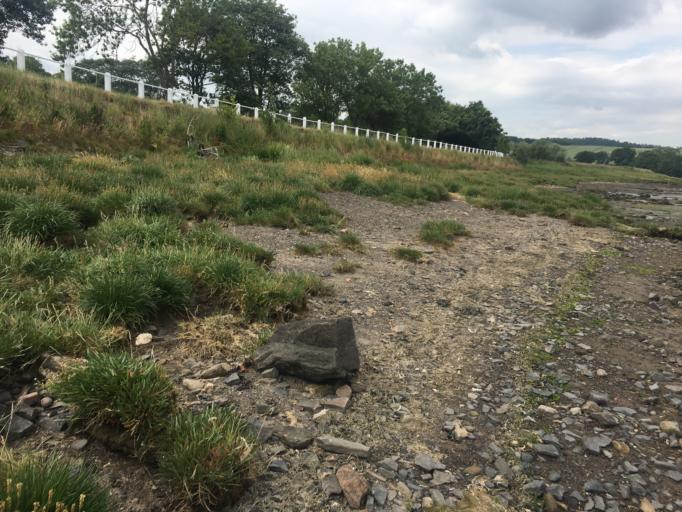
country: GB
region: England
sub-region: Northumberland
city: Bamburgh
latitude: 55.6044
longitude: -1.7646
